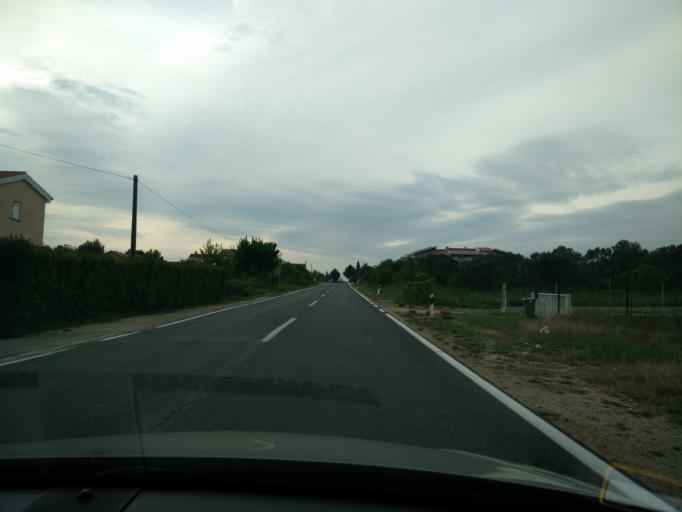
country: HR
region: Zadarska
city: Turanj
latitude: 43.9750
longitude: 15.3998
